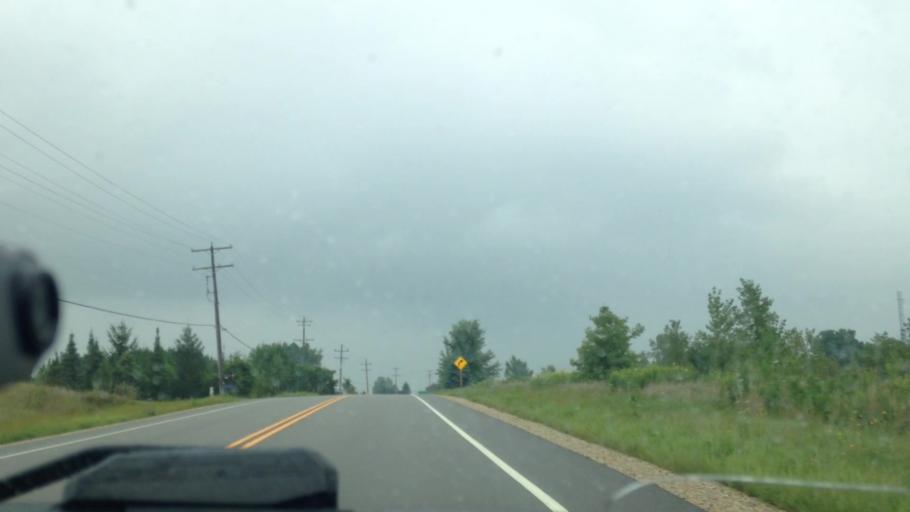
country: US
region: Wisconsin
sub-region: Washington County
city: Richfield
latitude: 43.2981
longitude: -88.2244
